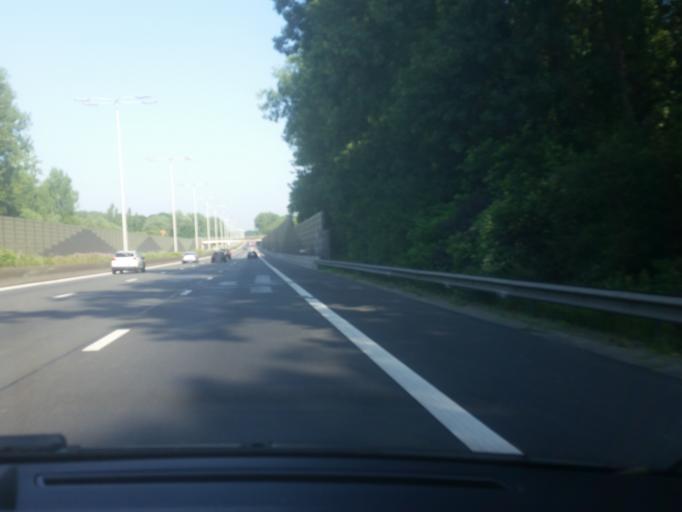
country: BE
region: Flanders
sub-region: Provincie Oost-Vlaanderen
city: Denderleeuw
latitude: 50.9057
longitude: 4.0797
